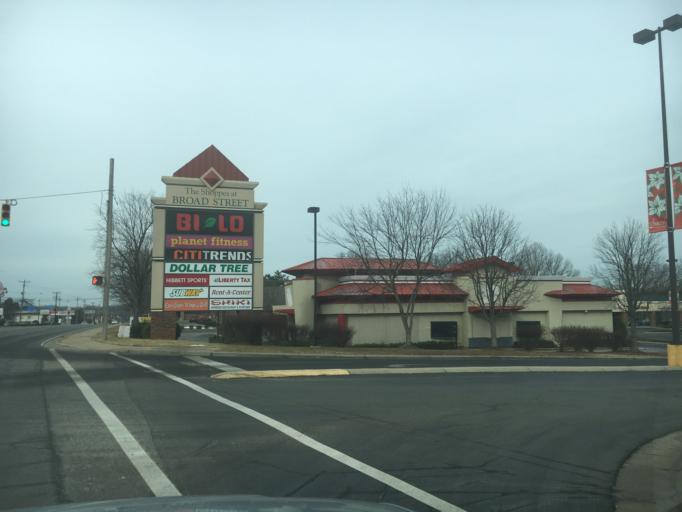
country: US
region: North Carolina
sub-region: Iredell County
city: Statesville
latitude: 35.7904
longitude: -80.8520
